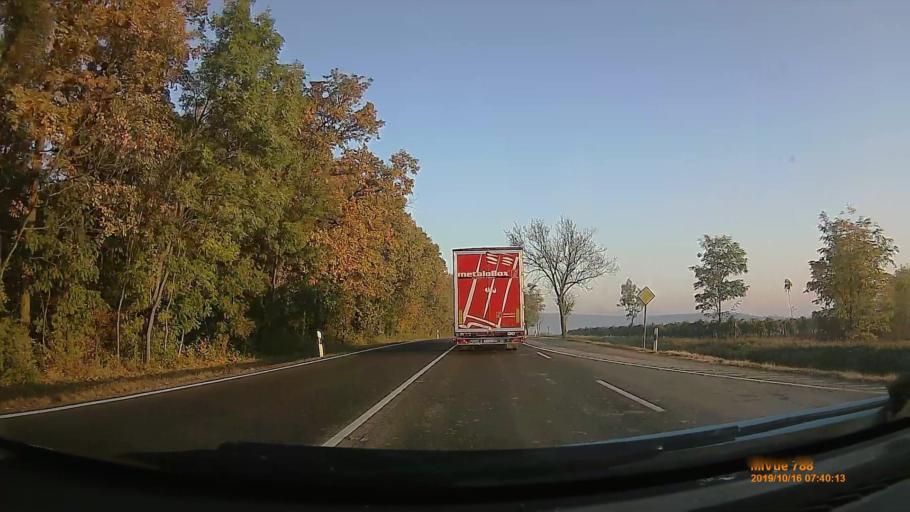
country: HU
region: Heves
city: Kerecsend
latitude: 47.8141
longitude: 20.3582
